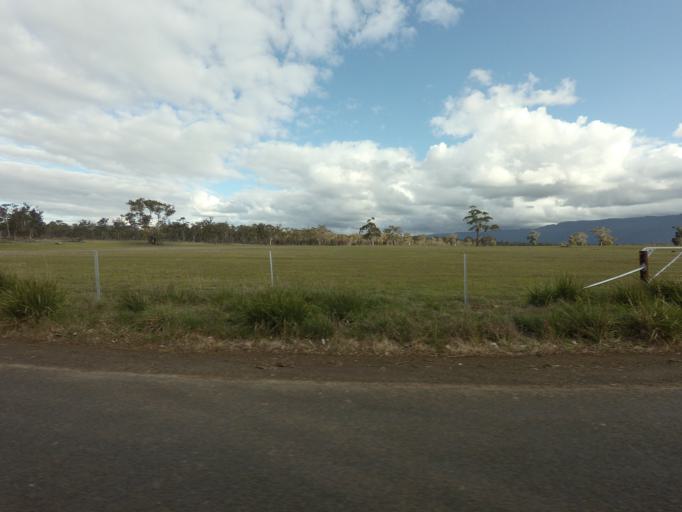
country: AU
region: Tasmania
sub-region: Northern Midlands
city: Evandale
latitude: -41.8653
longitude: 147.2737
